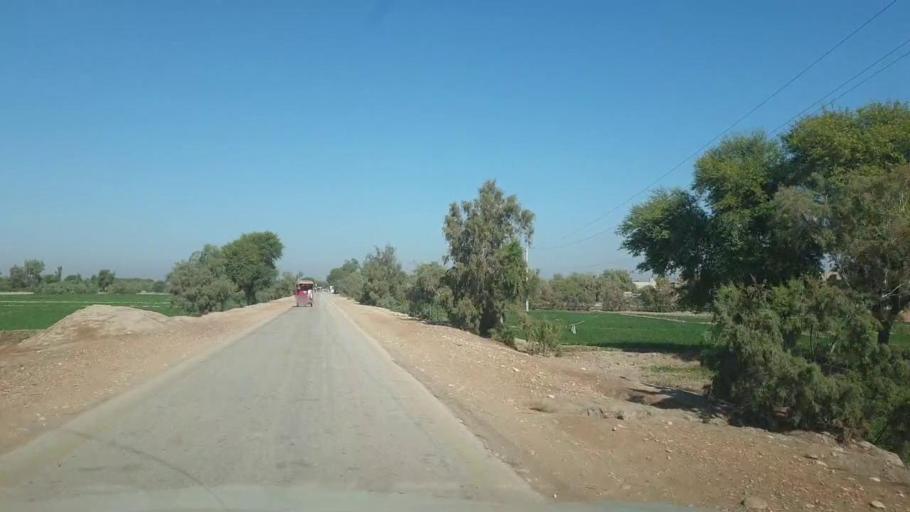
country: PK
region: Sindh
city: Bhan
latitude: 26.5435
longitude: 67.6349
